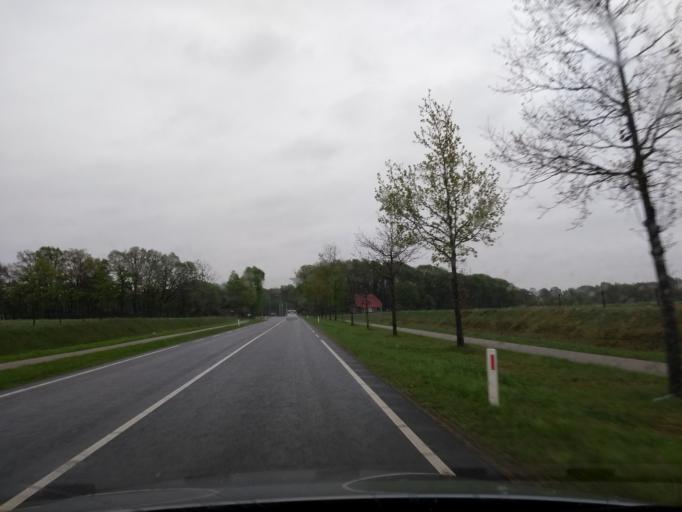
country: DE
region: Lower Saxony
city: Getelo
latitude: 52.3995
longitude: 6.8542
